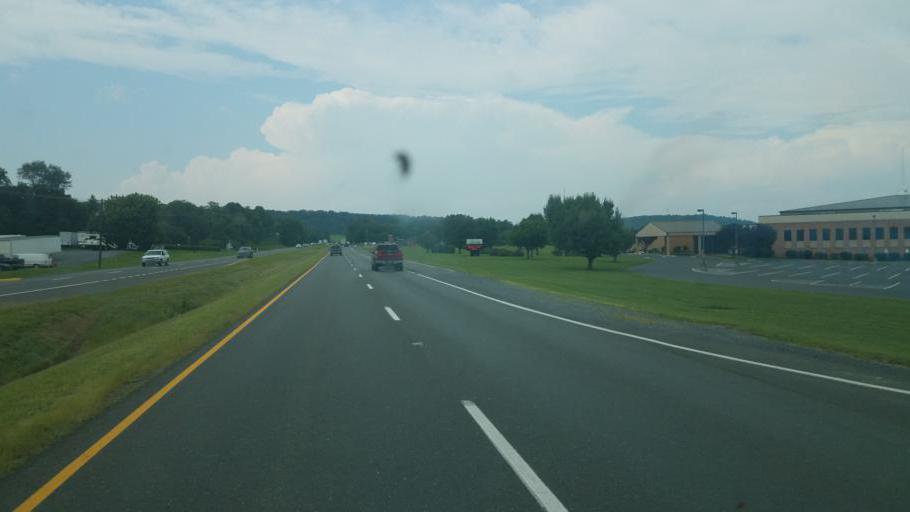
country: US
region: Virginia
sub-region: City of Winchester
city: Winchester
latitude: 39.2185
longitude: -78.1936
